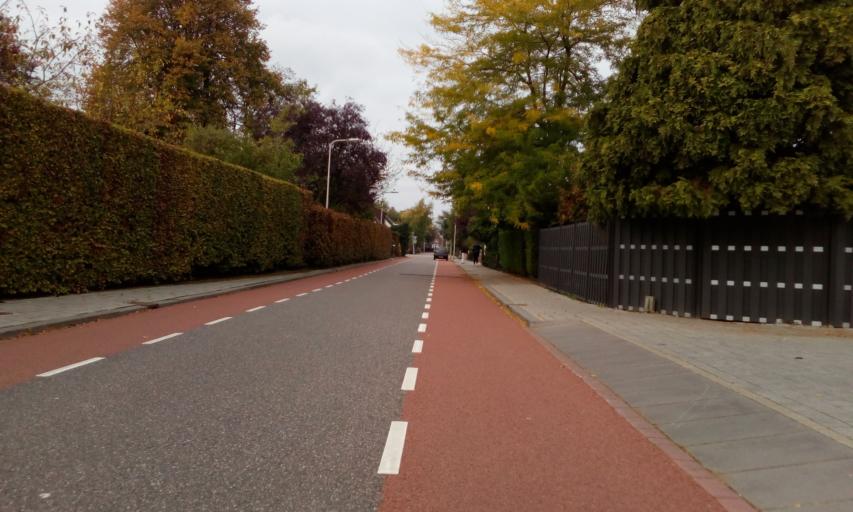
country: NL
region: South Holland
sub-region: Gemeente Albrandswaard
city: Rhoon
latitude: 51.8558
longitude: 4.4157
